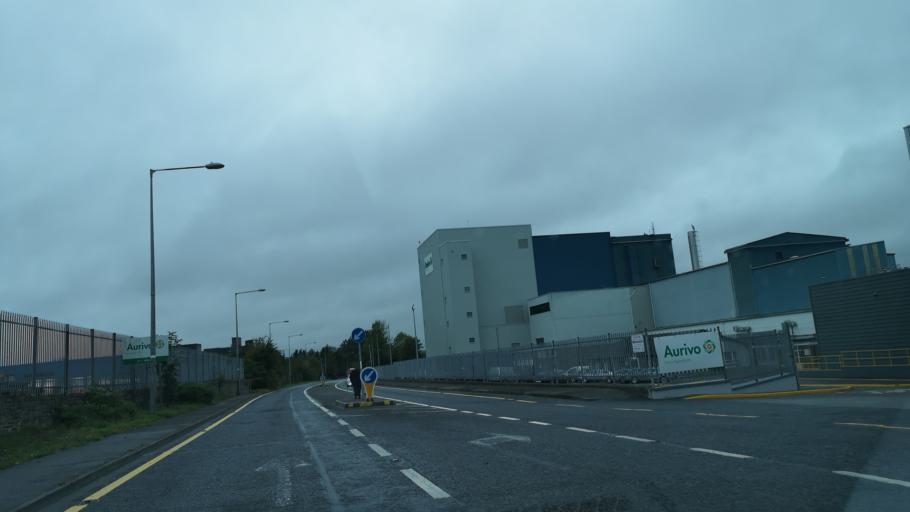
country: IE
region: Connaught
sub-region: Roscommon
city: Ballaghaderreen
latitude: 53.8970
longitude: -8.5673
